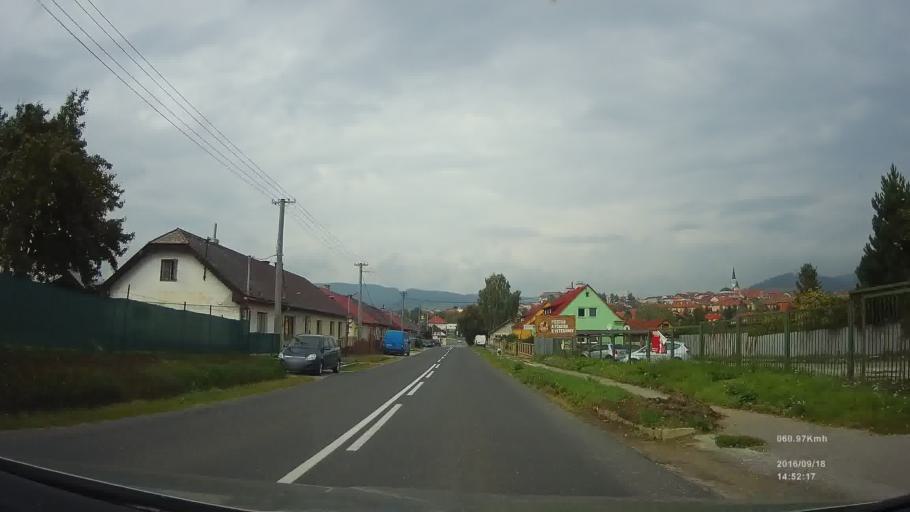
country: SK
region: Presovsky
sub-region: Okres Presov
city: Levoca
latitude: 49.0164
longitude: 20.5865
